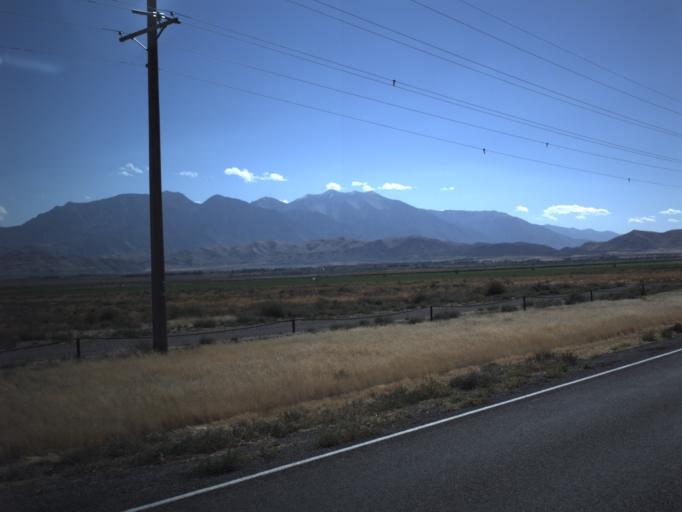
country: US
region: Utah
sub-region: Utah County
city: Genola
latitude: 40.0112
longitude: -111.9582
